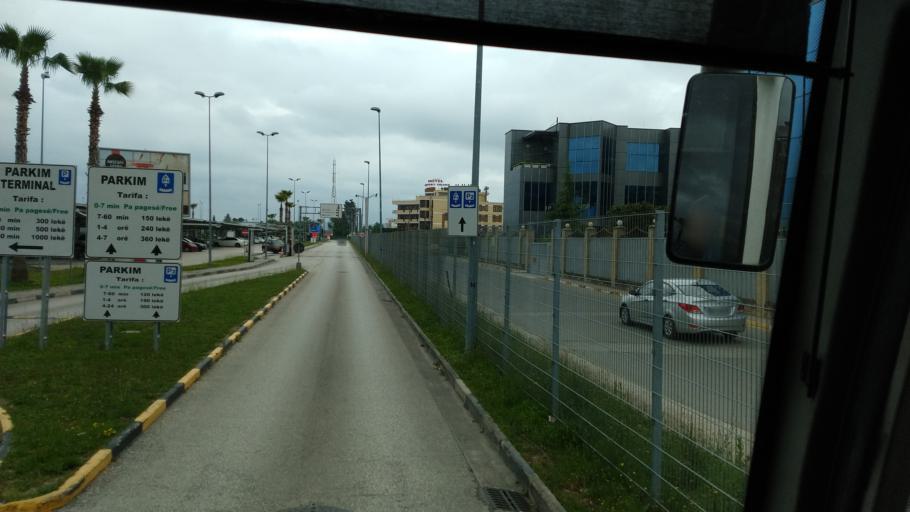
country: AL
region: Tirane
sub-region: Rrethi i Tiranes
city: Preze
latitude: 41.4187
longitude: 19.7127
